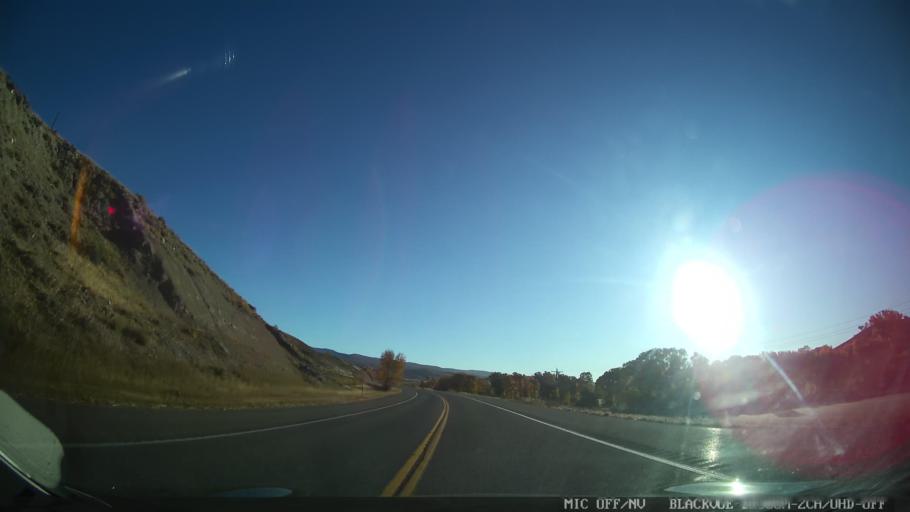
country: US
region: Colorado
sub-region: Grand County
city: Hot Sulphur Springs
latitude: 40.0630
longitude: -106.2403
